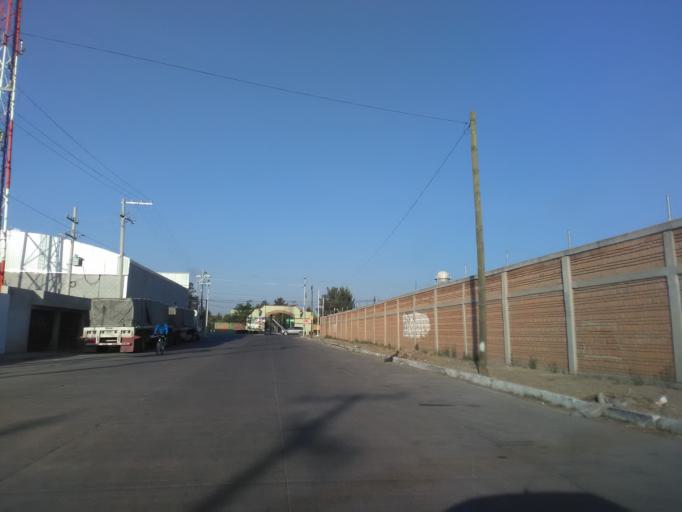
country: MX
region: Durango
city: Victoria de Durango
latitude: 24.0617
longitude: -104.6137
